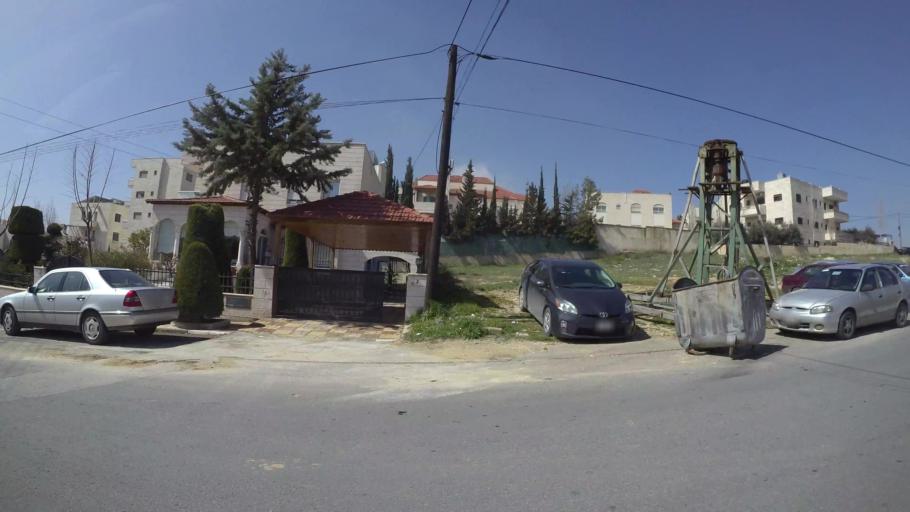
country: JO
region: Amman
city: Al Bunayyat ash Shamaliyah
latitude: 31.8979
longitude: 35.8763
